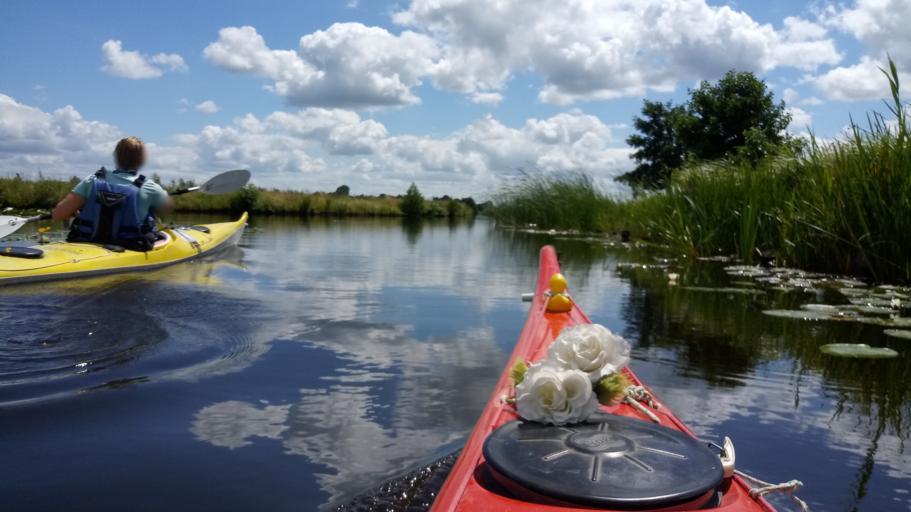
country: NL
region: Overijssel
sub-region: Gemeente Steenwijkerland
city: Wanneperveen
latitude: 52.7038
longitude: 6.0924
